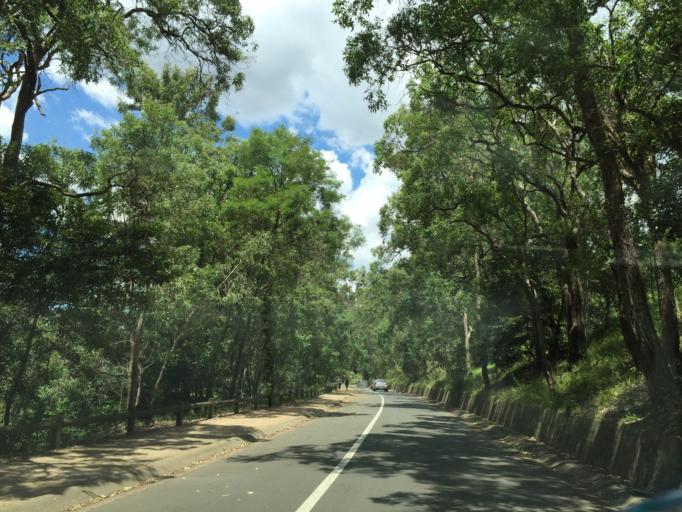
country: AU
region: New South Wales
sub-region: Parramatta
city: City of Parramatta
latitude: -33.8078
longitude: 150.9962
